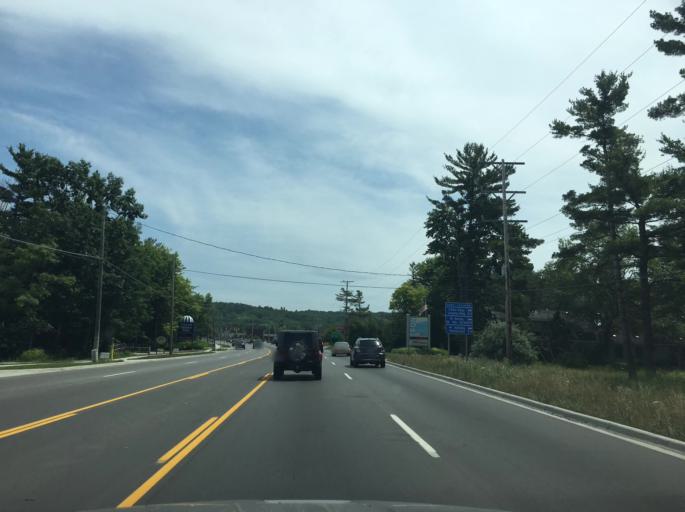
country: US
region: Michigan
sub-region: Grand Traverse County
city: Traverse City
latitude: 44.7461
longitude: -85.5319
